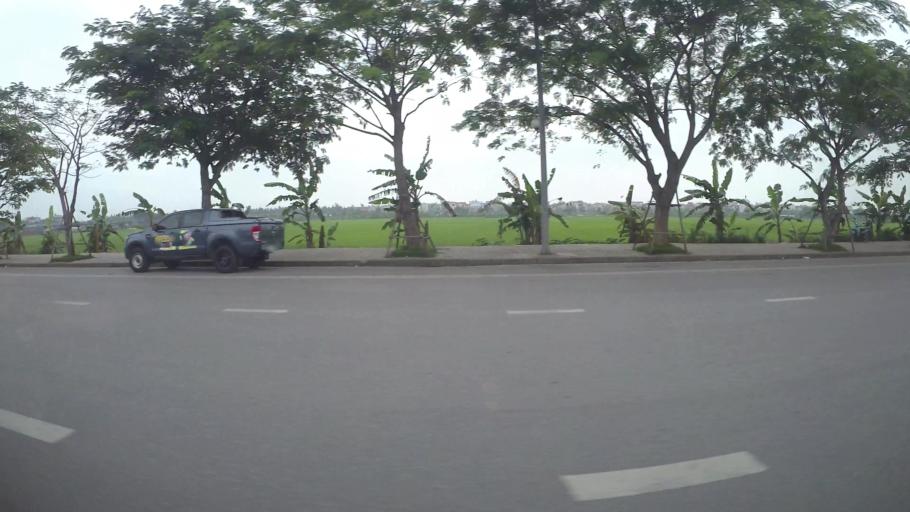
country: VN
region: Ha Noi
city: Trau Quy
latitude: 21.0516
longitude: 105.9171
